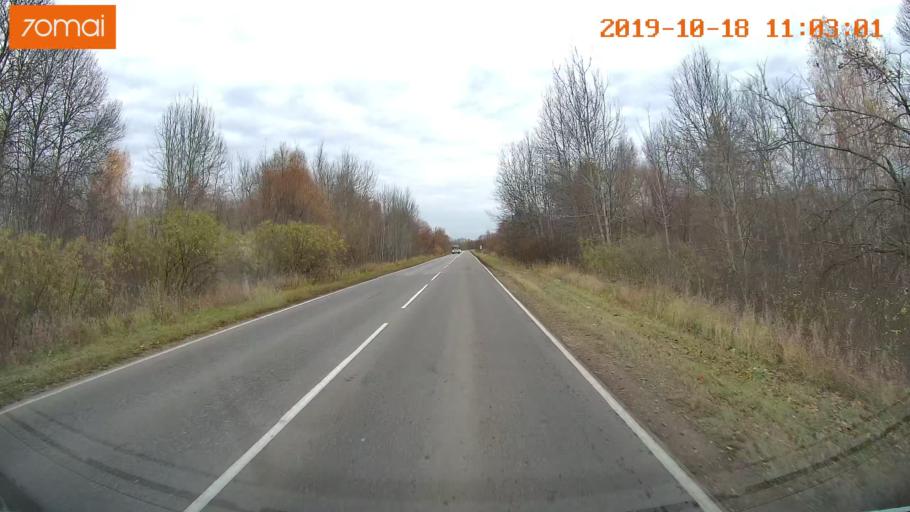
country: RU
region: Tula
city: Yepifan'
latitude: 53.8737
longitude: 38.5454
